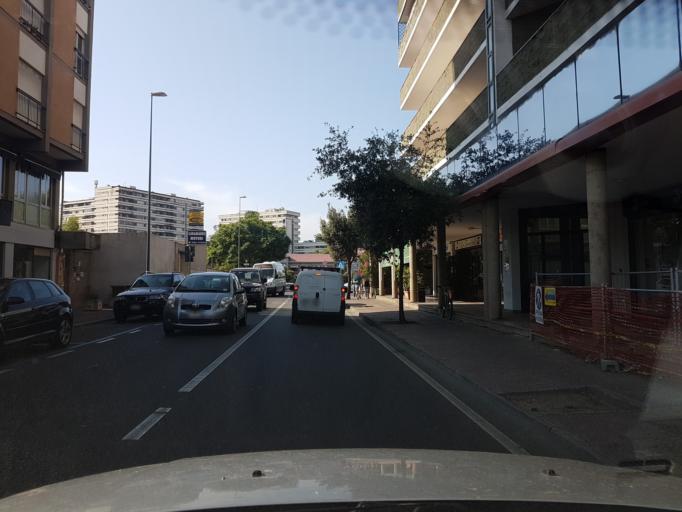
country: IT
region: Sardinia
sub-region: Provincia di Oristano
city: Oristano
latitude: 39.9038
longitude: 8.5884
